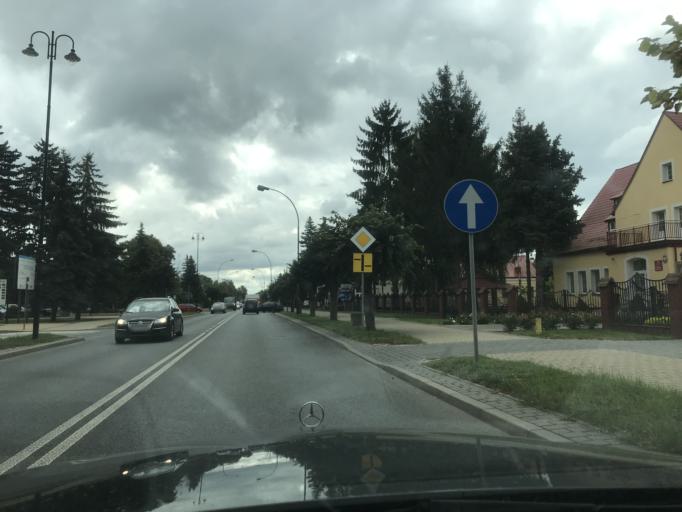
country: PL
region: Lublin Voivodeship
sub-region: Powiat janowski
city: Janow Lubelski
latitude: 50.7026
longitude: 22.4179
